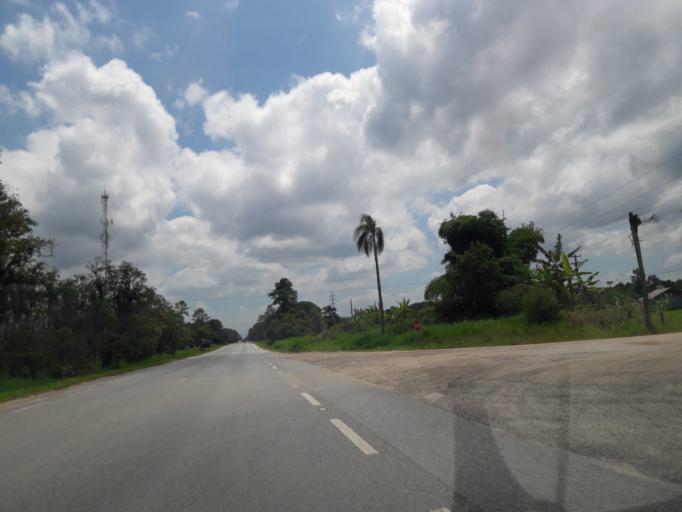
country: BR
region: Parana
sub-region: Pontal Do Parana
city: Pontal do Parana
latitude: -25.6424
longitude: -48.5323
